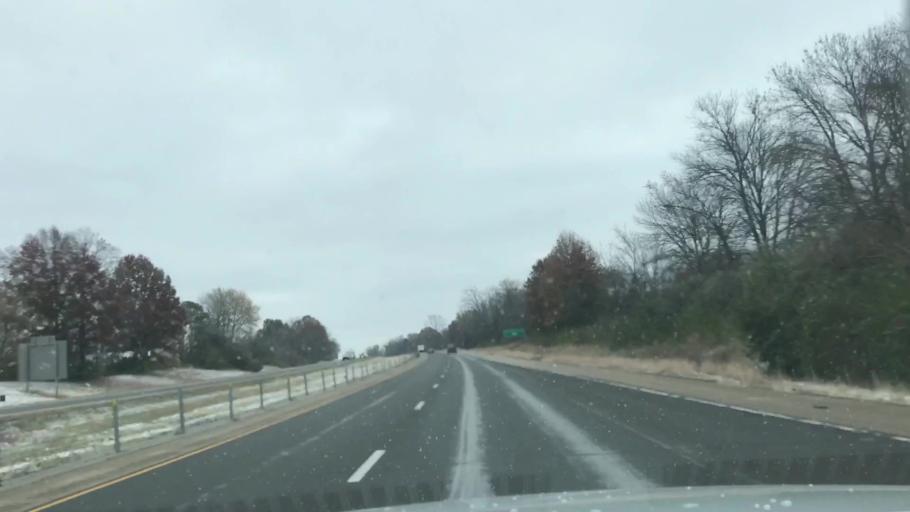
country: US
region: Illinois
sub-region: Madison County
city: Maryville
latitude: 38.7543
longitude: -89.9512
